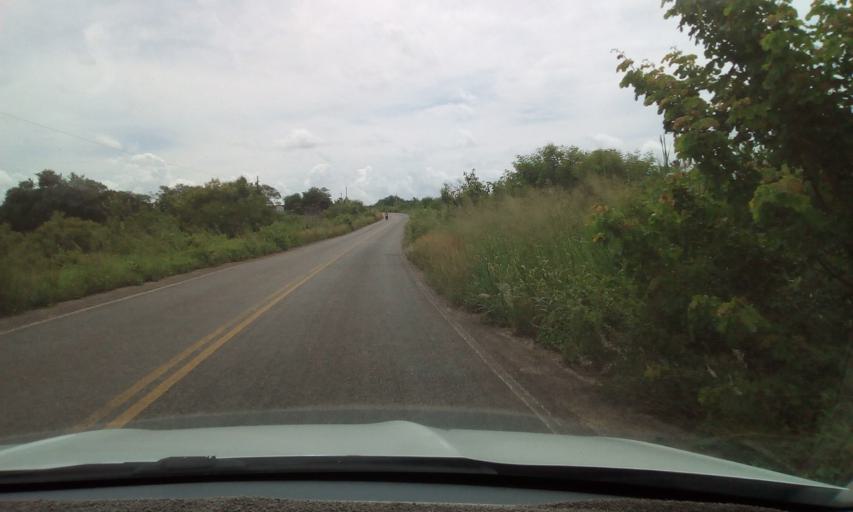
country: BR
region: Paraiba
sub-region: Mari
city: Mari
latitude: -7.1191
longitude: -35.3430
